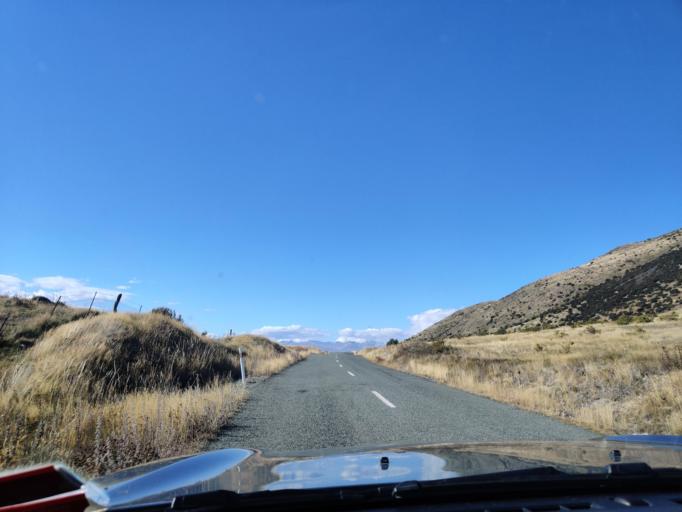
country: NZ
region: Canterbury
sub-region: Timaru District
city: Pleasant Point
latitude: -43.9825
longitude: 170.4583
